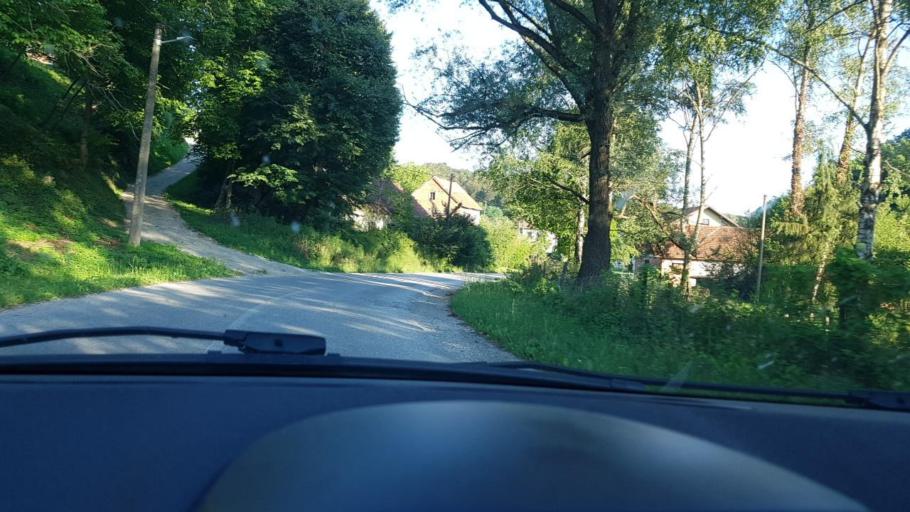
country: HR
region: Krapinsko-Zagorska
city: Bedekovcina
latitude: 46.0651
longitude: 16.0031
